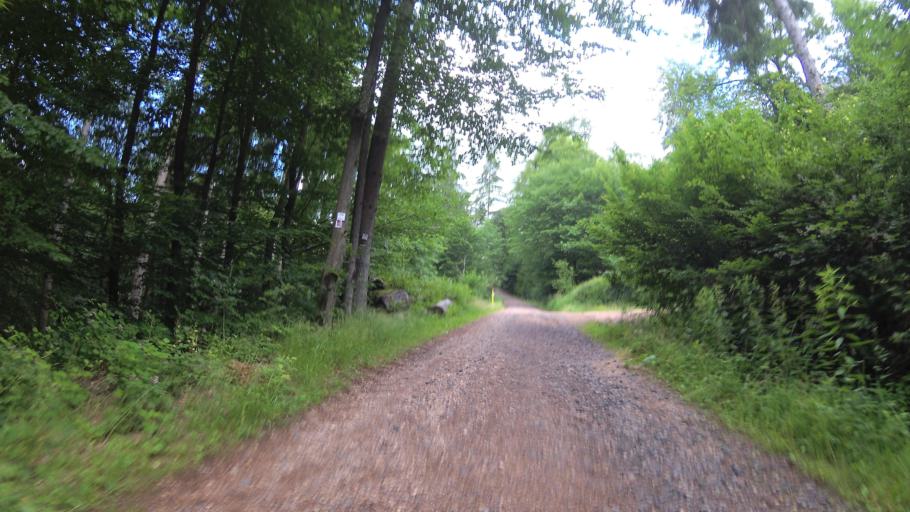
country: DE
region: Saarland
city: Nonnweiler
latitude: 49.6165
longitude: 6.9743
